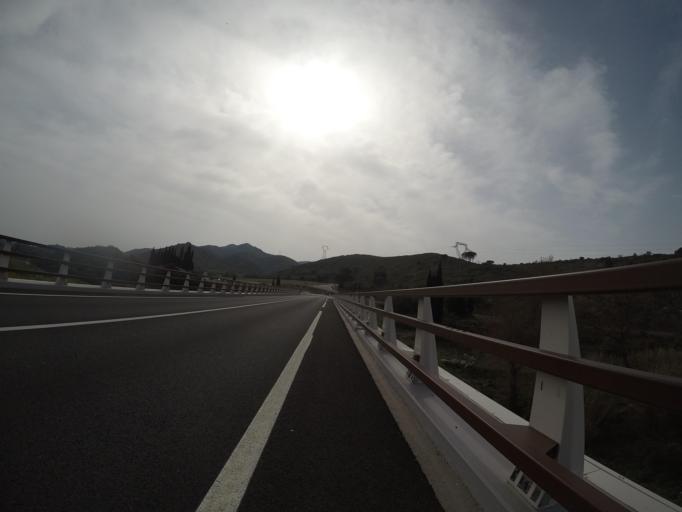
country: FR
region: Languedoc-Roussillon
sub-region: Departement des Pyrenees-Orientales
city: Estagel
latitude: 42.7762
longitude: 2.7085
